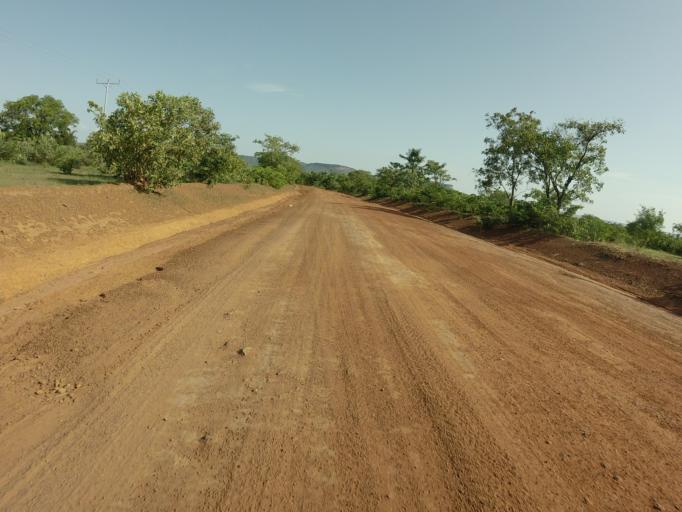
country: GH
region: Upper East
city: Bawku
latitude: 10.6901
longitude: -0.2159
